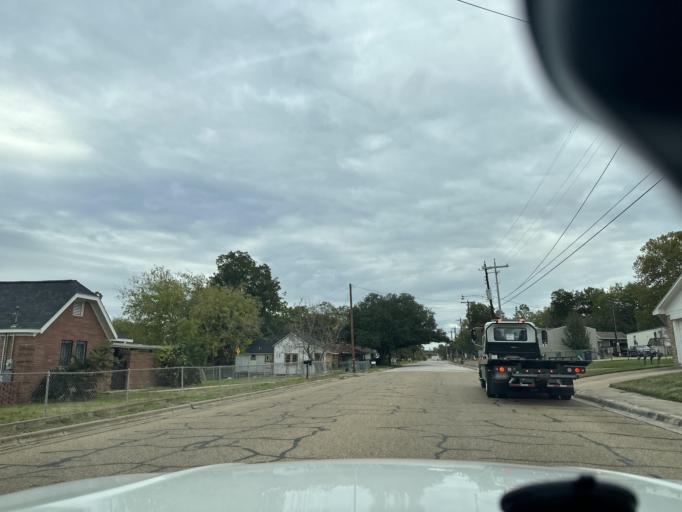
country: US
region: Texas
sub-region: Washington County
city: Brenham
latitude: 30.1692
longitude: -96.4047
